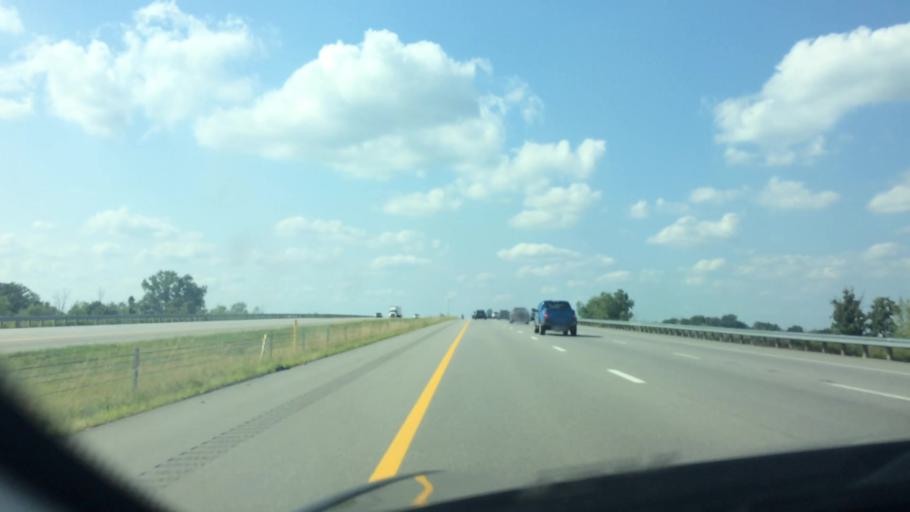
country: US
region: Ohio
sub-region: Wood County
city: Bowling Green
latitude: 41.4351
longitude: -83.6176
